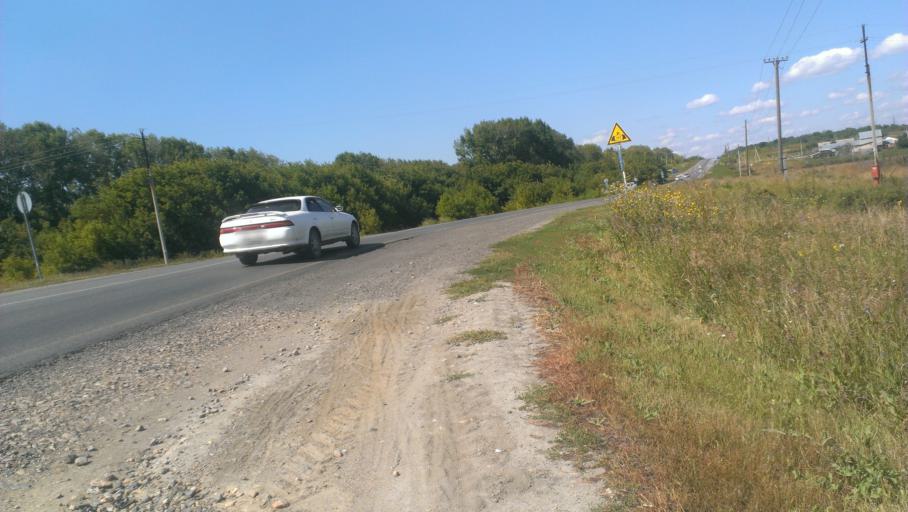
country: RU
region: Altai Krai
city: Gon'ba
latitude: 53.4001
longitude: 83.5849
